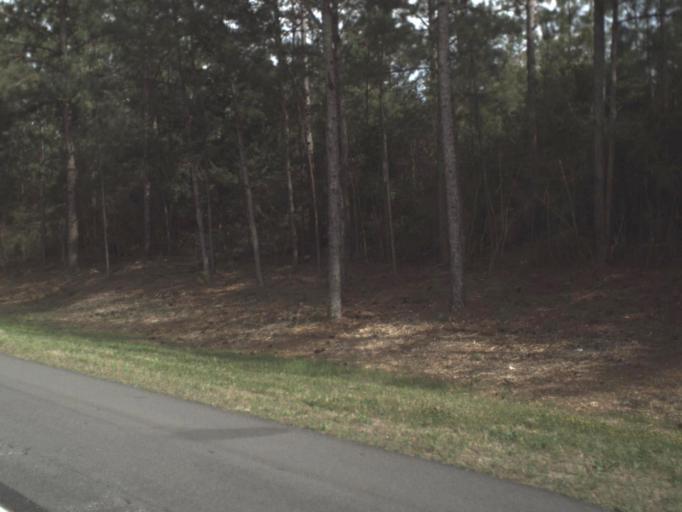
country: US
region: Florida
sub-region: Walton County
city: DeFuniak Springs
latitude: 30.6945
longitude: -85.9991
